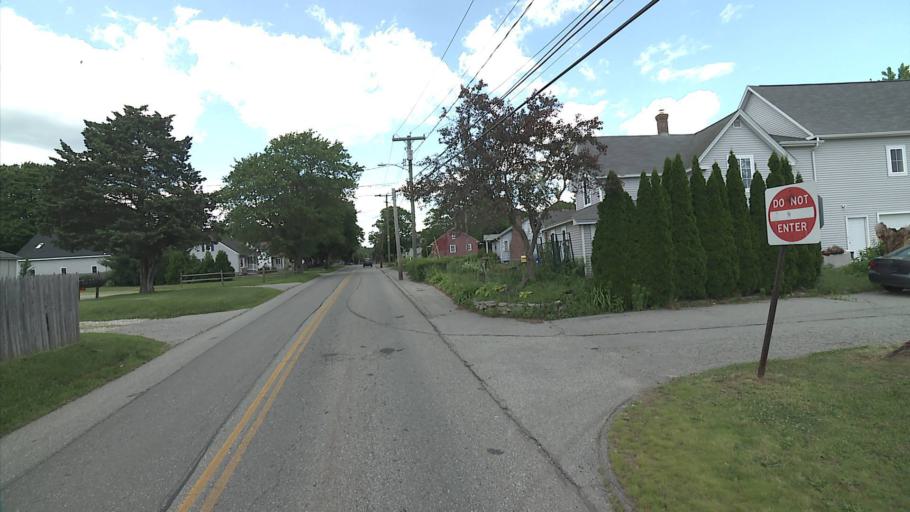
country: US
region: Connecticut
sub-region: New London County
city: Poquonock Bridge
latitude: 41.3427
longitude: -72.0390
